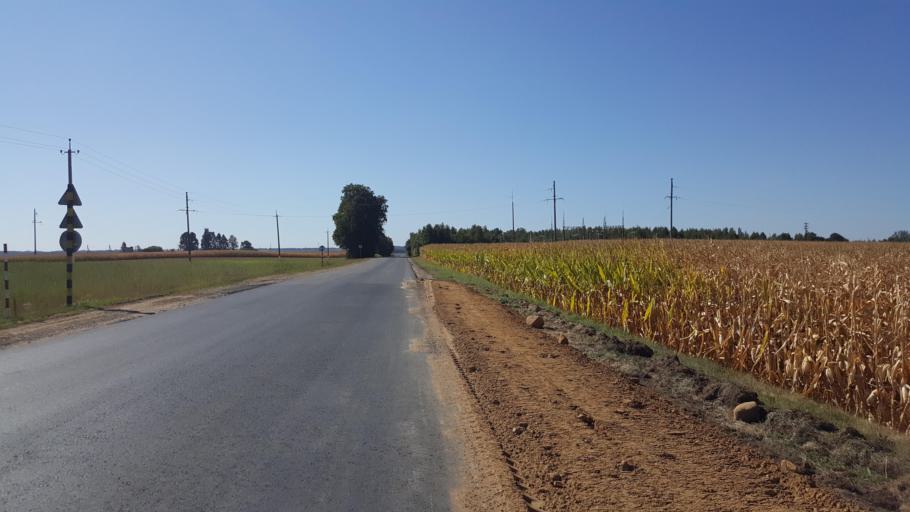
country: BY
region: Brest
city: Charnawchytsy
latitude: 52.2876
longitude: 23.6045
